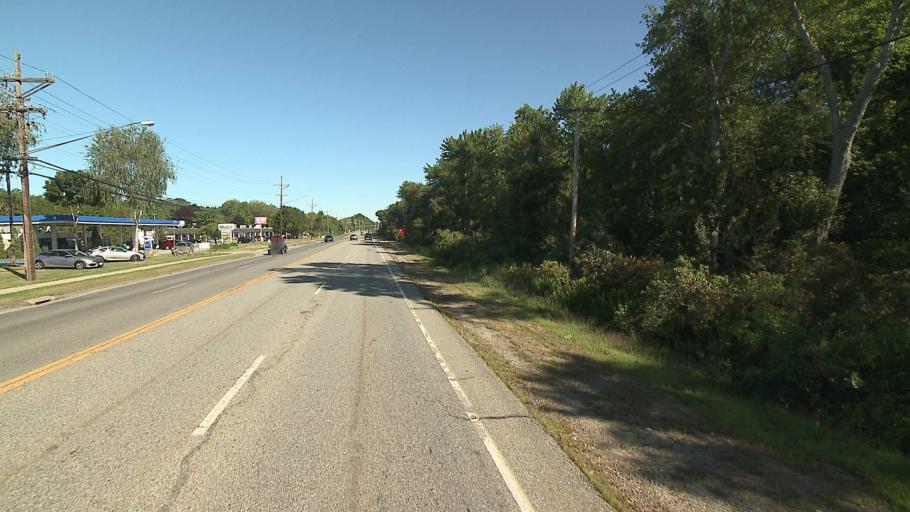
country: US
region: Connecticut
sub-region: New London County
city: Conning Towers-Nautilus Park
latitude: 41.3763
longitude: -72.0743
